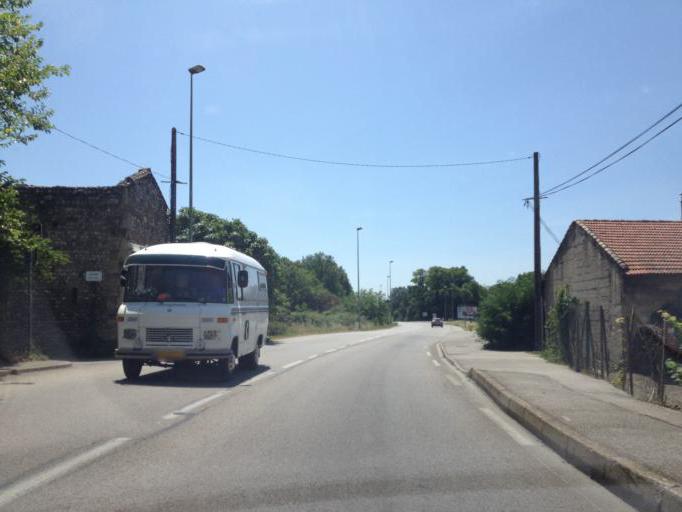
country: FR
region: Rhone-Alpes
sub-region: Departement de l'Ardeche
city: Guilherand-Granges
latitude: 44.9263
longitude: 4.8823
